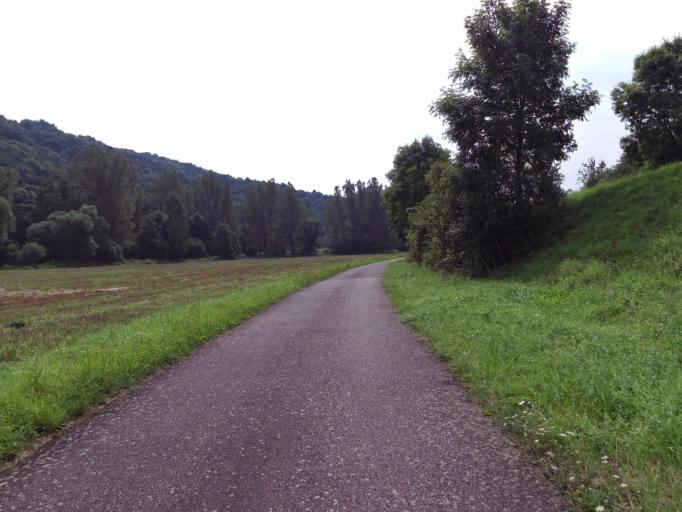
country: DE
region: Rheinland-Pfalz
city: Kalkofen
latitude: 49.7410
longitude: 7.8213
